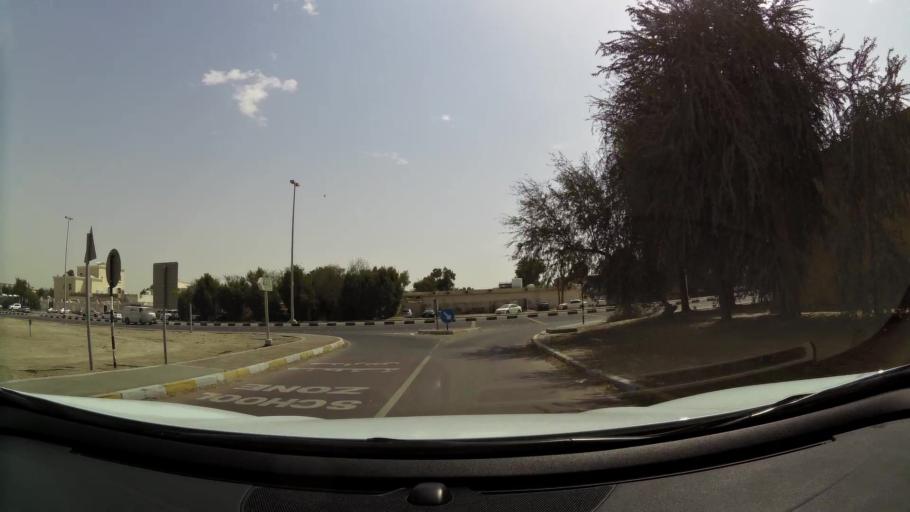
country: AE
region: Abu Dhabi
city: Abu Dhabi
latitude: 24.2905
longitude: 54.6391
